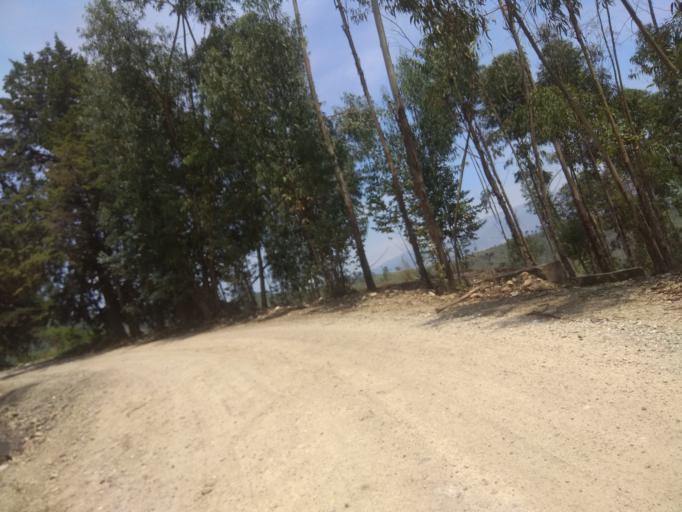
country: CO
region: Boyaca
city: Socha Viejo
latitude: 5.9790
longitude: -72.7255
